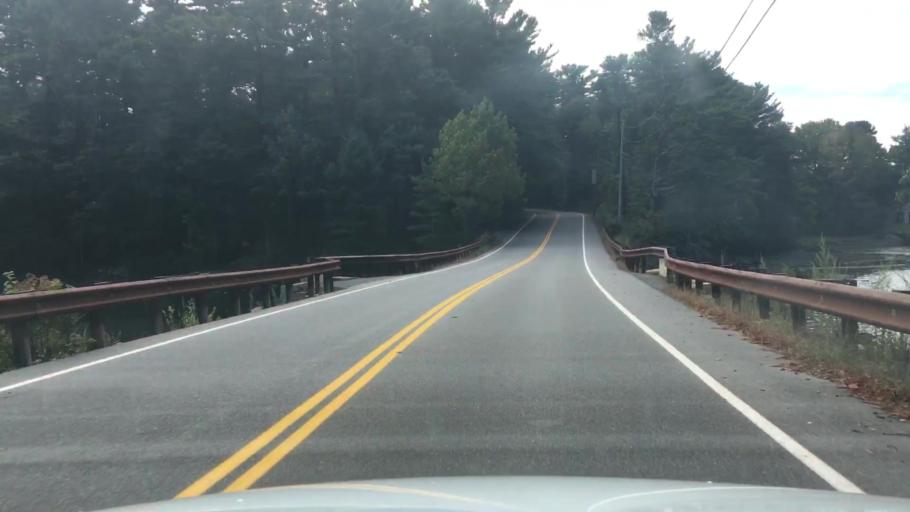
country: US
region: Maine
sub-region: York County
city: Kittery Point
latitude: 43.0849
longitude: -70.7116
